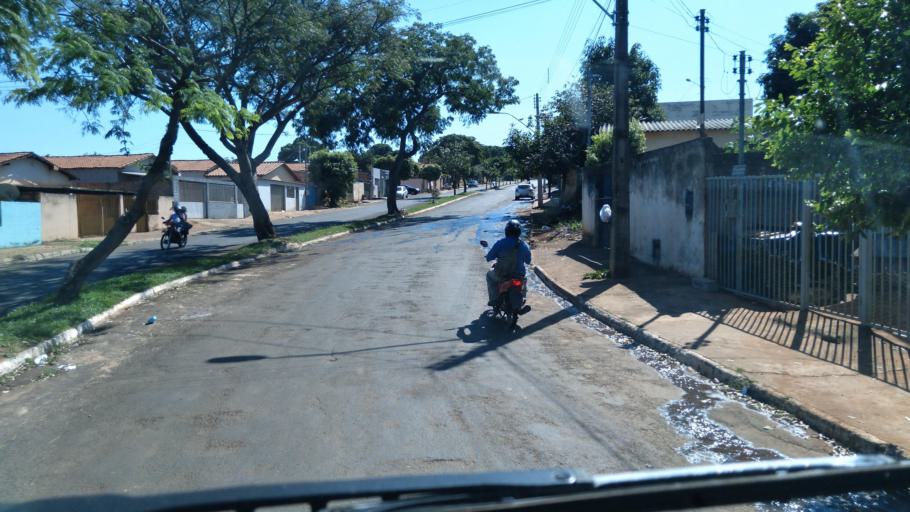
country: BR
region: Goias
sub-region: Mineiros
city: Mineiros
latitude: -17.5719
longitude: -52.5696
